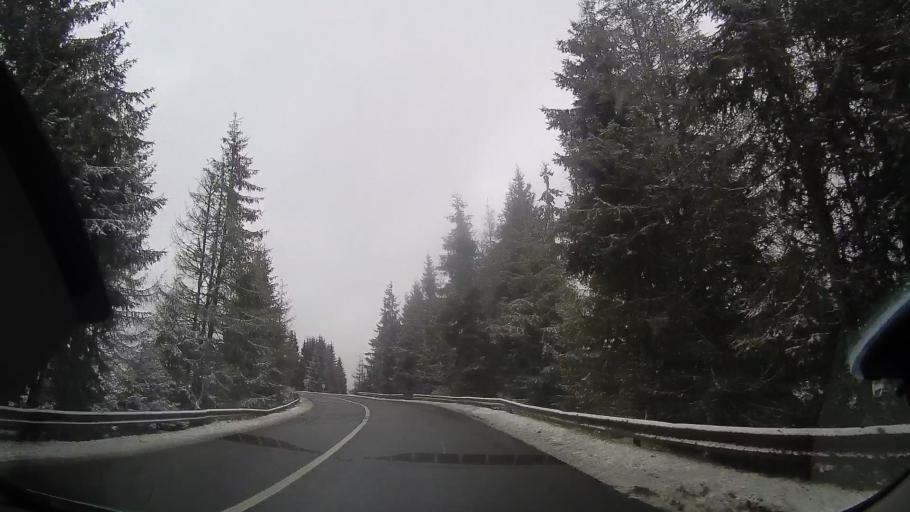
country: RO
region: Cluj
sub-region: Comuna Belis
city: Belis
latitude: 46.6781
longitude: 23.0445
